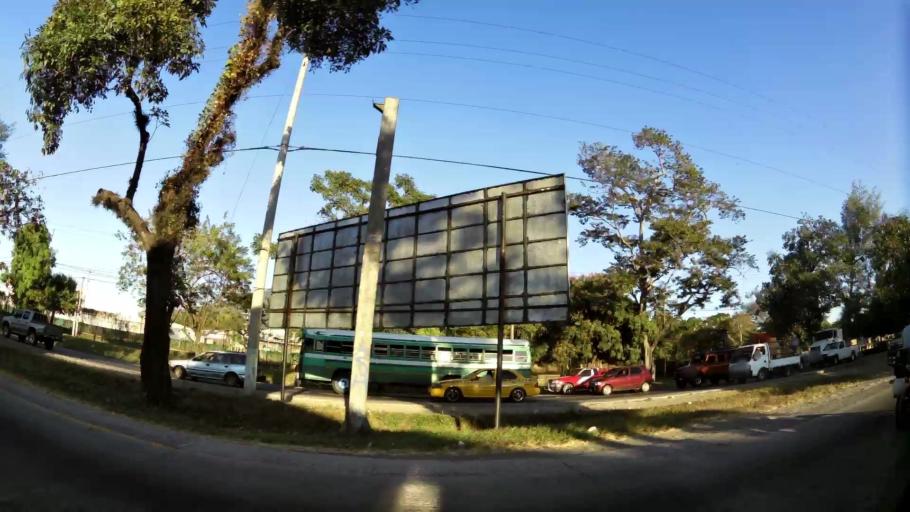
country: SV
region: La Libertad
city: Santa Tecla
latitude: 13.7259
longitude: -89.3579
